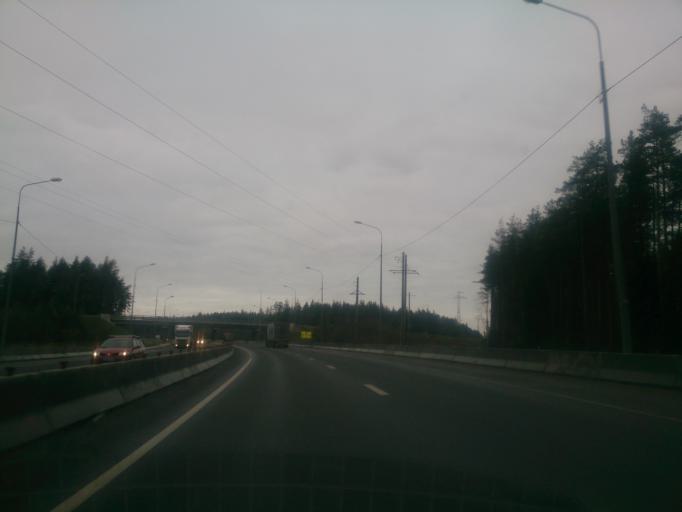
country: RU
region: Leningrad
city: Nurma
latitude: 59.4920
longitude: 30.9645
